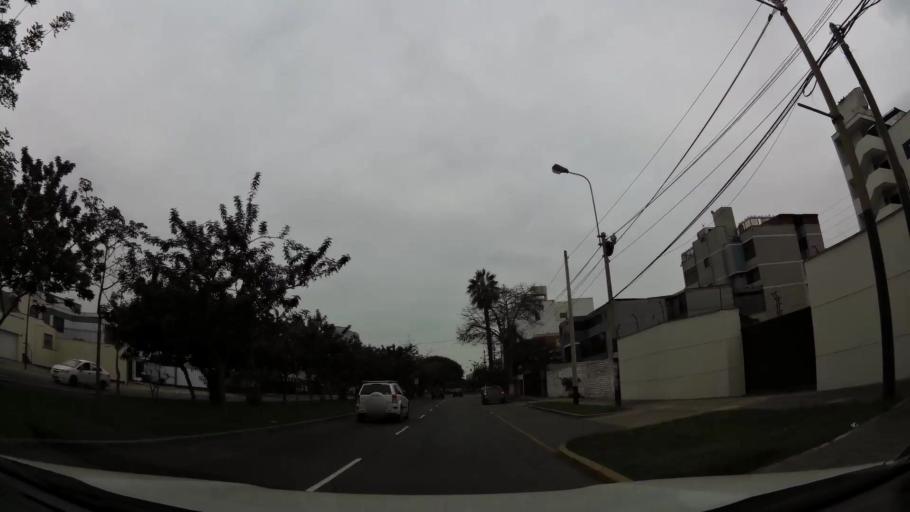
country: PE
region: Lima
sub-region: Lima
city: San Luis
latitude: -12.0944
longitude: -77.0134
